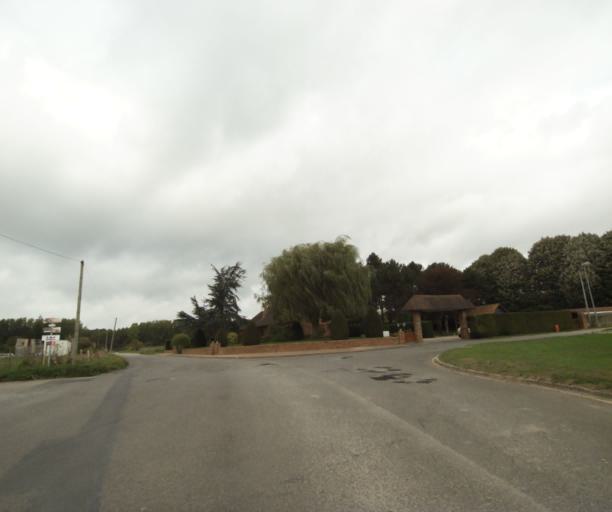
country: FR
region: Nord-Pas-de-Calais
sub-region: Departement du Pas-de-Calais
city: Etaples
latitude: 50.5217
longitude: 1.6599
